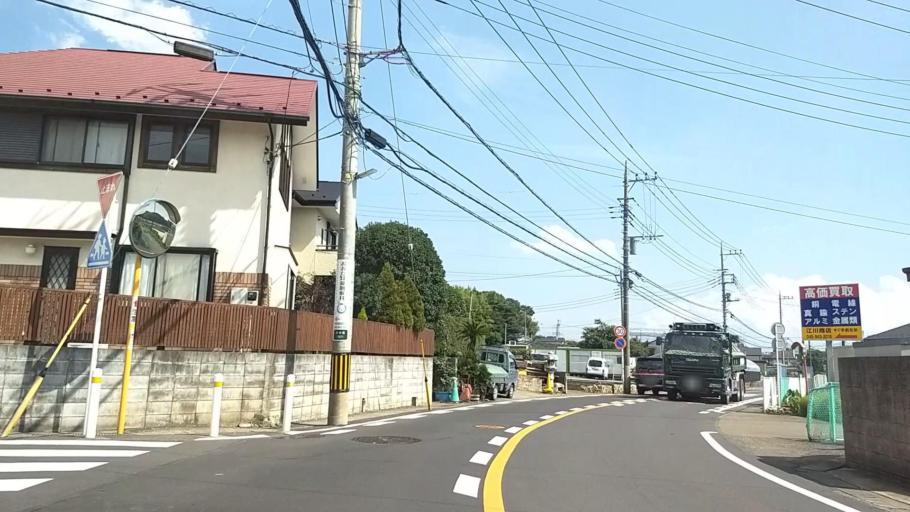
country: JP
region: Kanagawa
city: Yokohama
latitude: 35.5293
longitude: 139.5870
